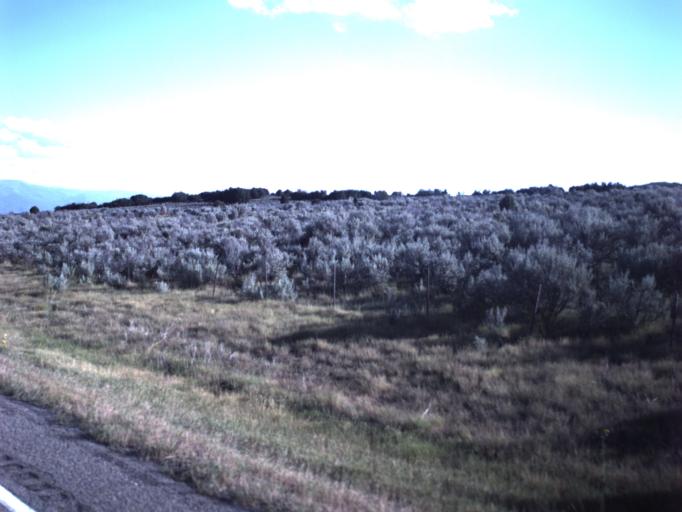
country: US
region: Utah
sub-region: Sanpete County
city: Fairview
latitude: 39.6929
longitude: -111.4610
